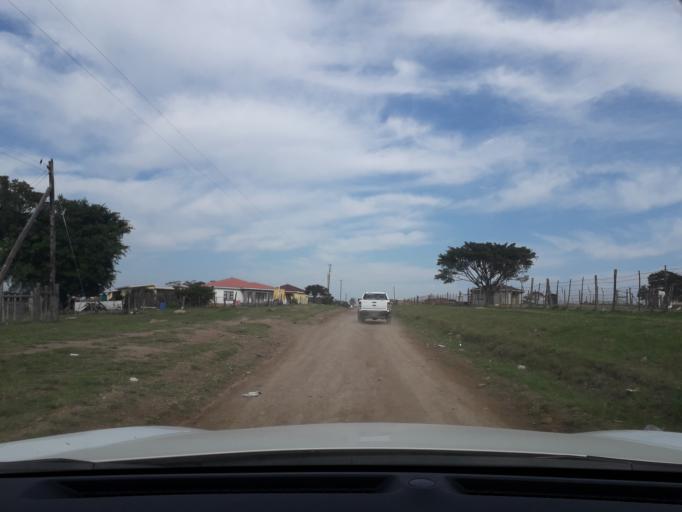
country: ZA
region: Eastern Cape
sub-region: Buffalo City Metropolitan Municipality
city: Bhisho
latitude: -32.9875
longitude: 27.3603
